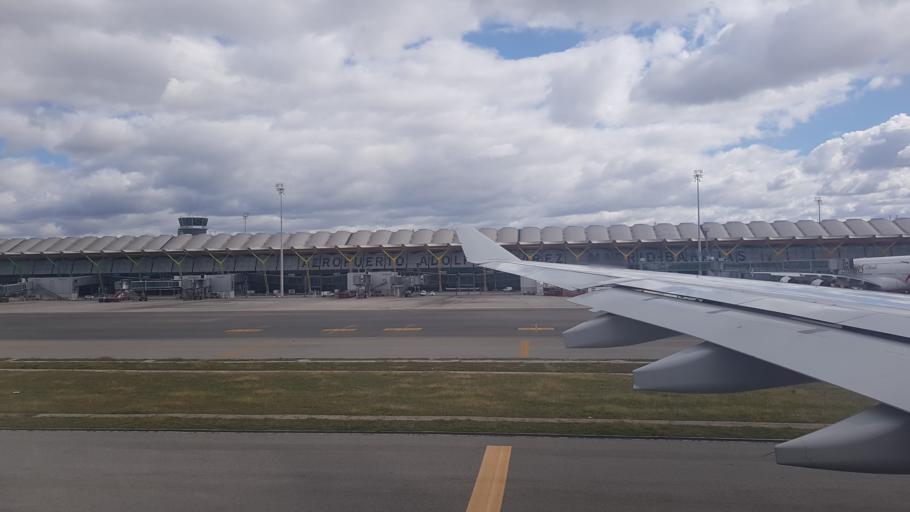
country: ES
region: Madrid
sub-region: Provincia de Madrid
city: Barajas de Madrid
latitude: 40.4945
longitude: -3.5711
